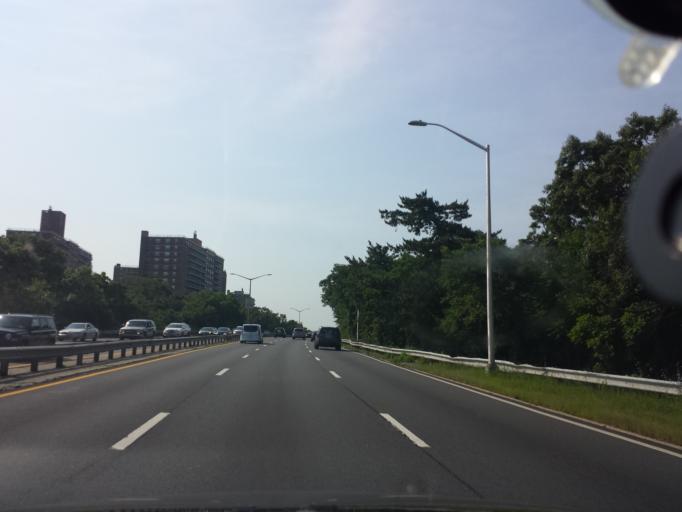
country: US
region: New York
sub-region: Kings County
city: Bensonhurst
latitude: 40.5909
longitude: -73.9938
